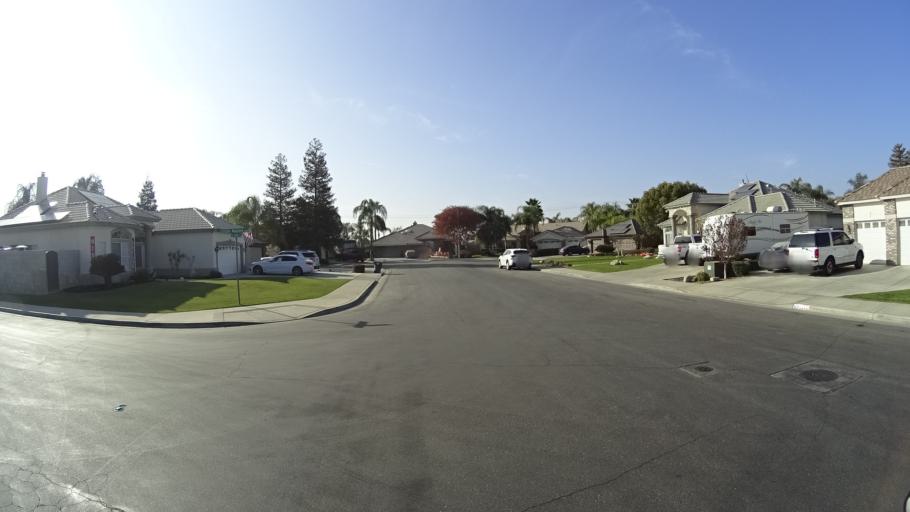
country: US
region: California
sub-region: Kern County
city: Rosedale
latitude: 35.3584
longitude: -119.1617
